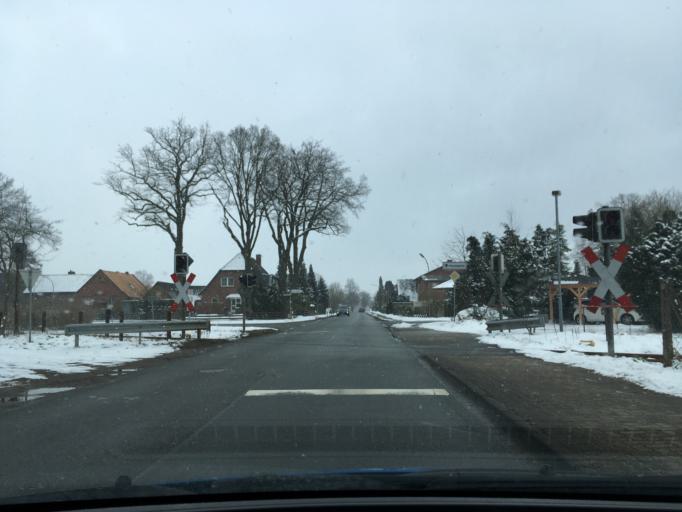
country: DE
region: Lower Saxony
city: Winsen
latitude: 53.3295
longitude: 10.2015
